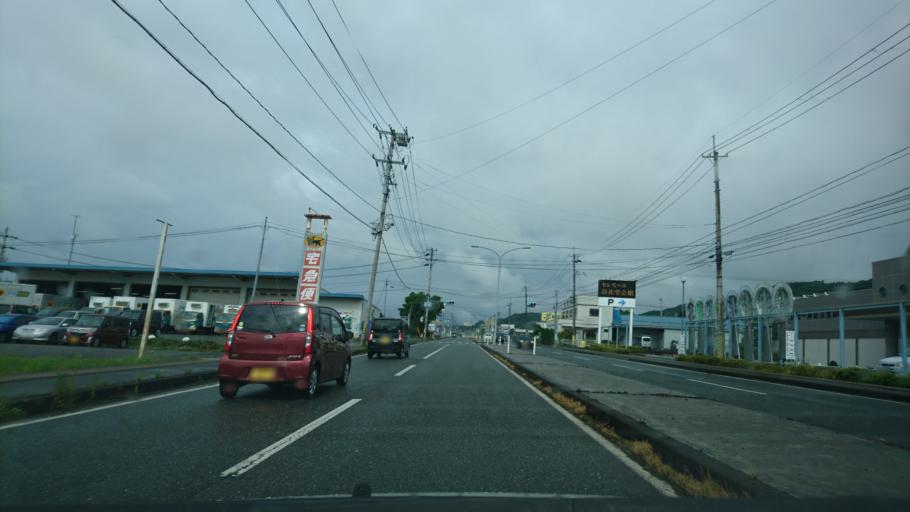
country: JP
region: Iwate
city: Ichinoseki
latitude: 38.9396
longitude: 141.0963
